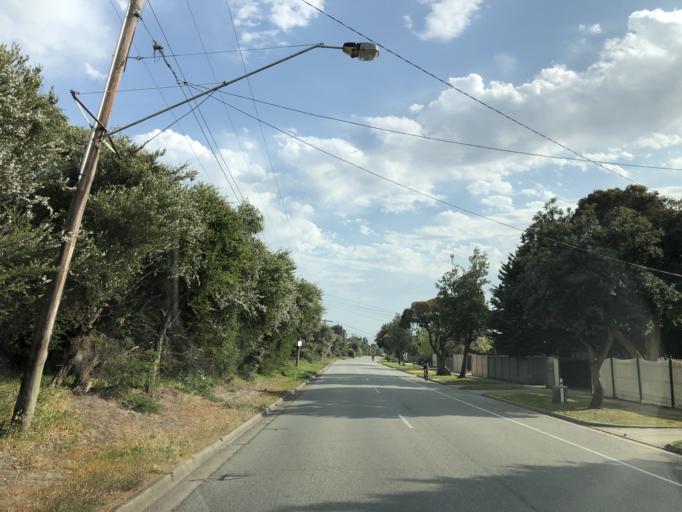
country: AU
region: Victoria
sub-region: Kingston
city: Carrum
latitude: -38.0871
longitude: 145.1275
